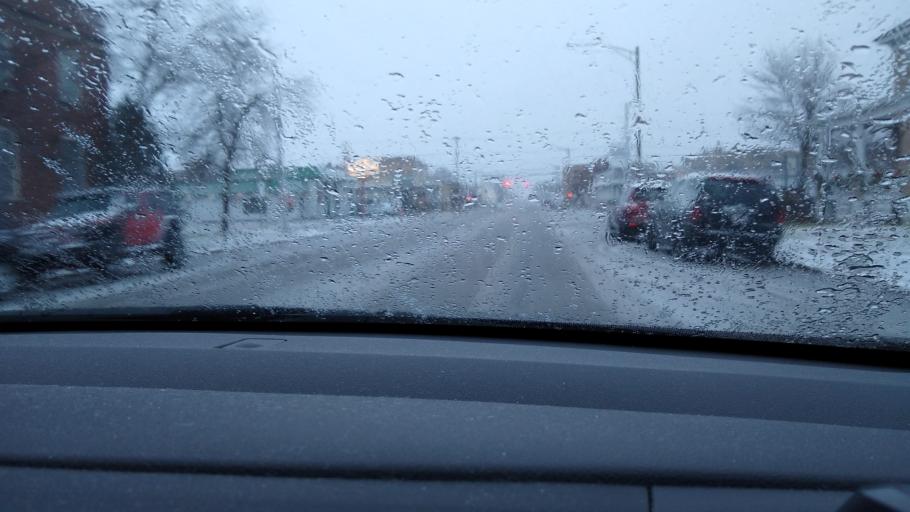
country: US
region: Michigan
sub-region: Delta County
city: Escanaba
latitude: 45.7442
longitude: -87.0612
